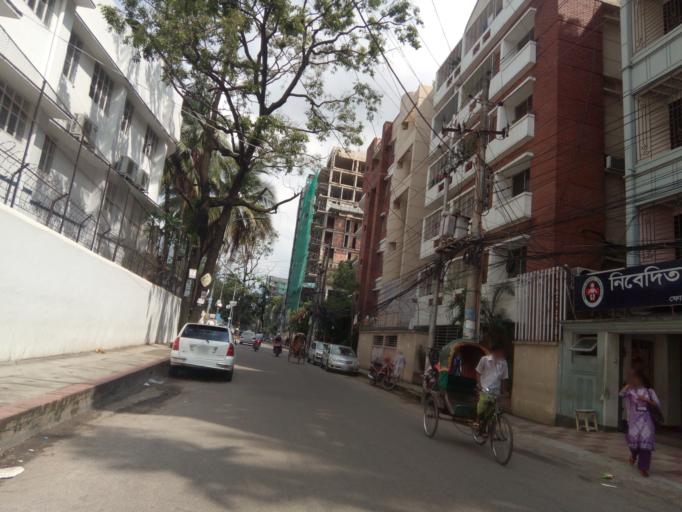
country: BD
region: Dhaka
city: Azimpur
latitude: 23.7497
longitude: 90.3748
